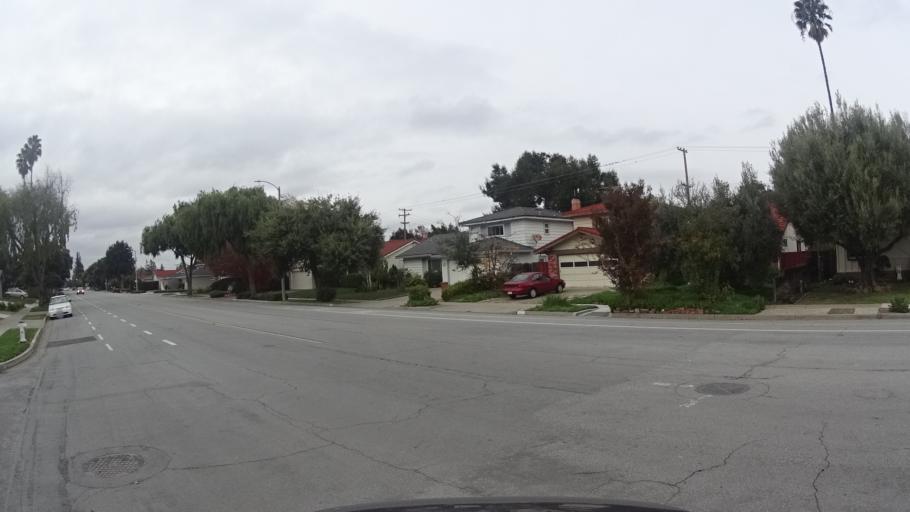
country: US
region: California
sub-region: Santa Clara County
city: Sunnyvale
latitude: 37.3594
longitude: -122.0464
